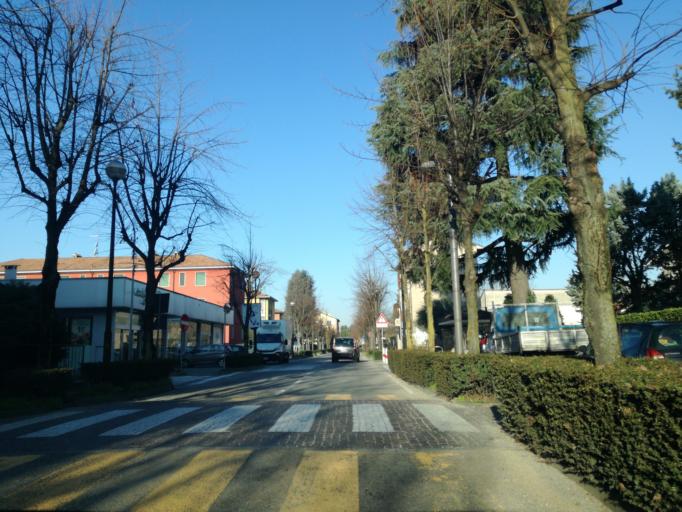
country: IT
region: Lombardy
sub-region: Provincia di Monza e Brianza
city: Vimercate
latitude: 45.6168
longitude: 9.3640
